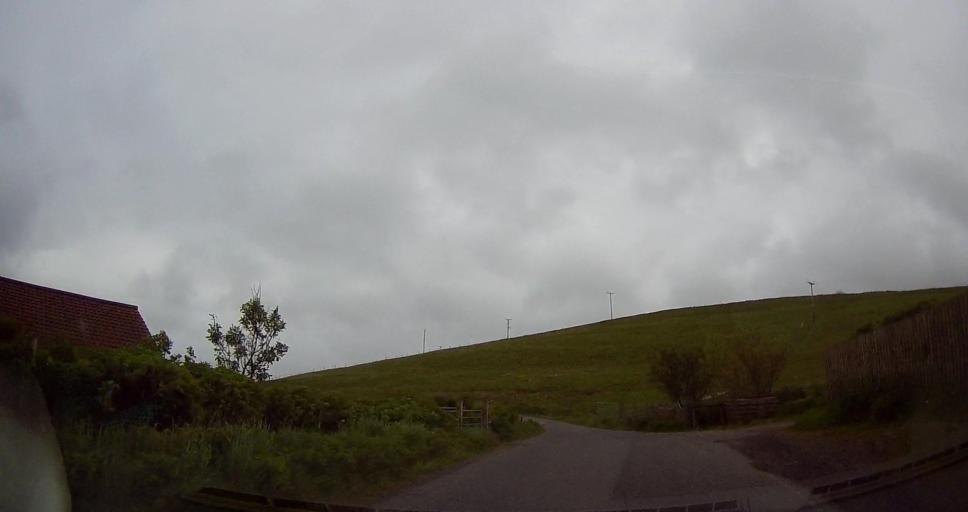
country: GB
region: Scotland
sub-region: Shetland Islands
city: Lerwick
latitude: 60.3719
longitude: -1.3821
